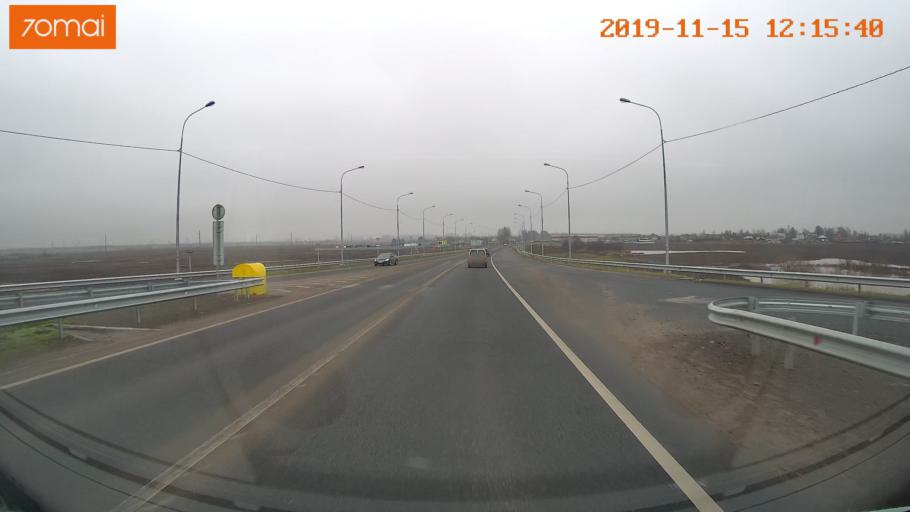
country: RU
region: Vologda
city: Vologda
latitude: 59.1615
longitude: 39.8162
